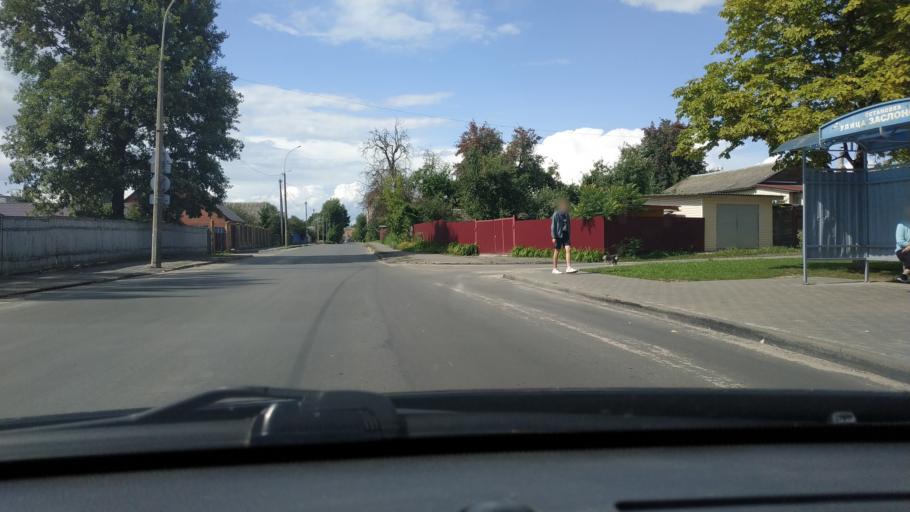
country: BY
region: Mogilev
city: Buynichy
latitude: 53.8999
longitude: 30.2922
